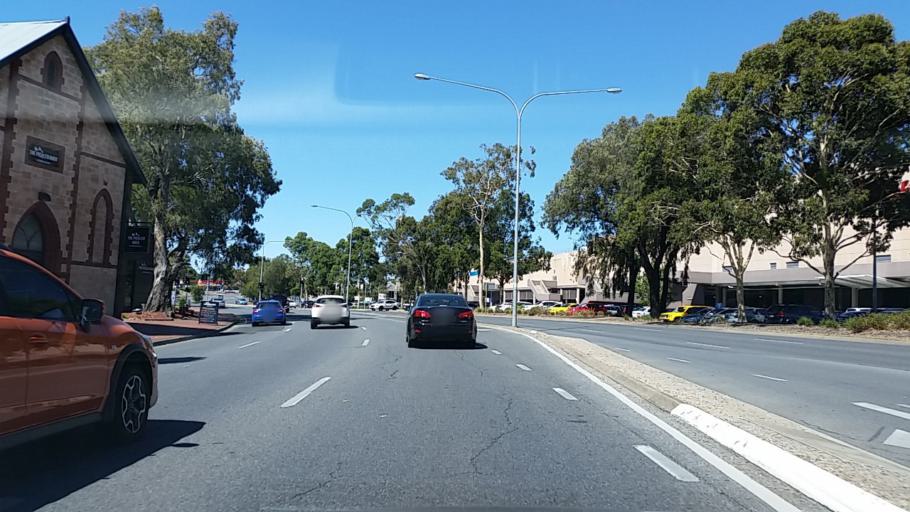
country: AU
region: South Australia
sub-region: Tea Tree Gully
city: Modbury
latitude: -34.8312
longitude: 138.6888
